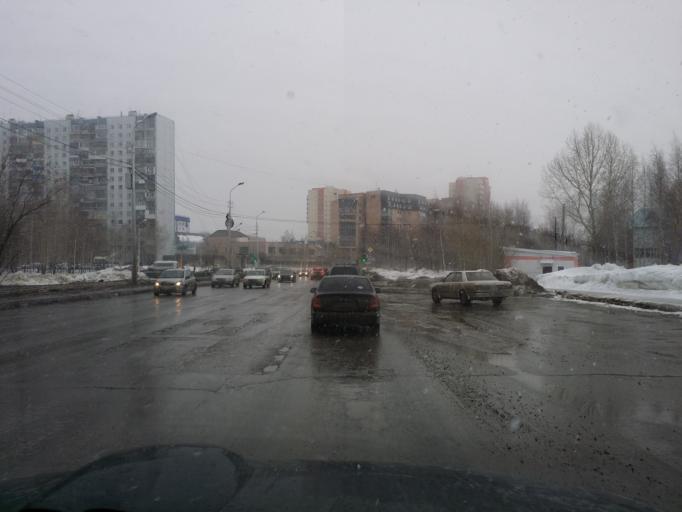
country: RU
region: Khanty-Mansiyskiy Avtonomnyy Okrug
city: Nizhnevartovsk
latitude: 60.9310
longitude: 76.5664
